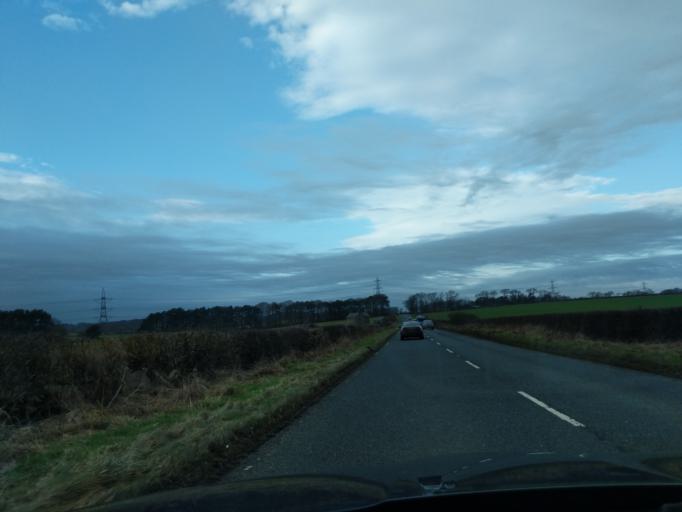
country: GB
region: England
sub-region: Northumberland
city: Meldon
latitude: 55.0981
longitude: -1.8204
